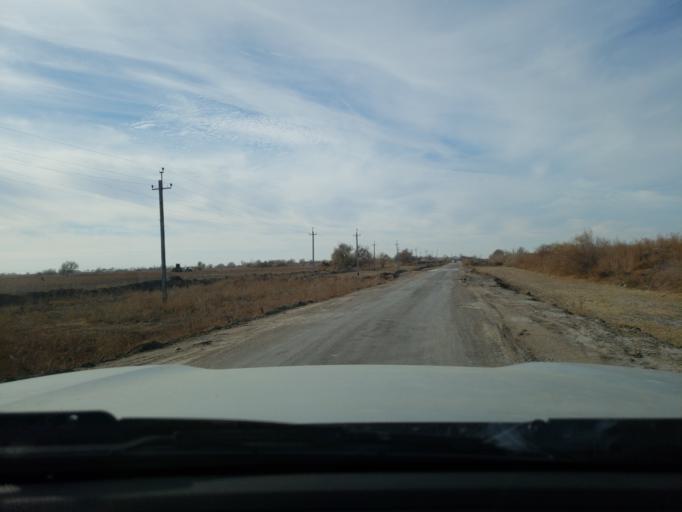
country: TM
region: Dasoguz
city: Dasoguz
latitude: 41.8493
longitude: 59.8868
